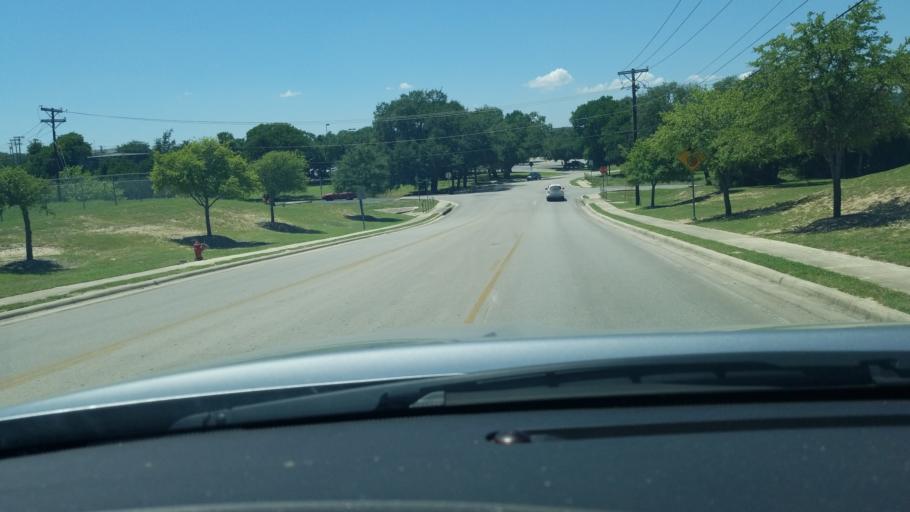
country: US
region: Texas
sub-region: Comal County
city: Bulverde
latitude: 29.7958
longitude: -98.4242
